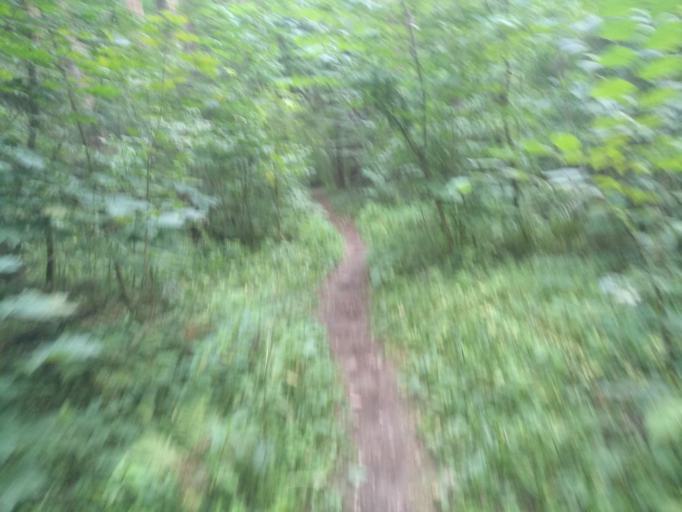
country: RU
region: Moskovskaya
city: Dedovsk
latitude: 55.8733
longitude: 37.0922
